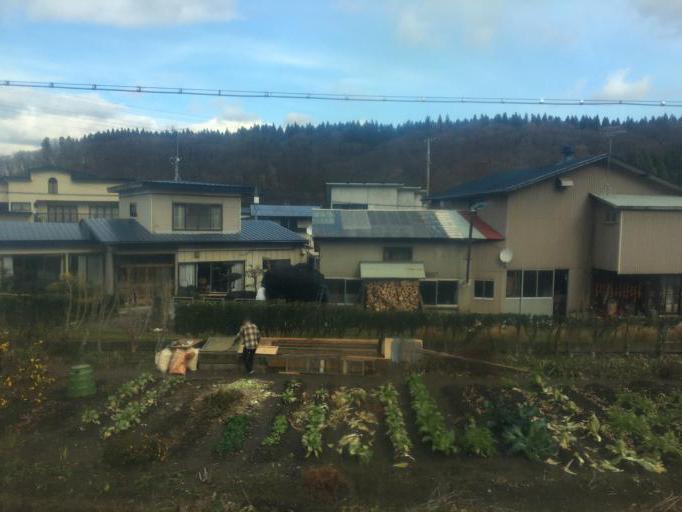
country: JP
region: Akita
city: Noshiromachi
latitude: 40.2037
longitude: 140.1196
